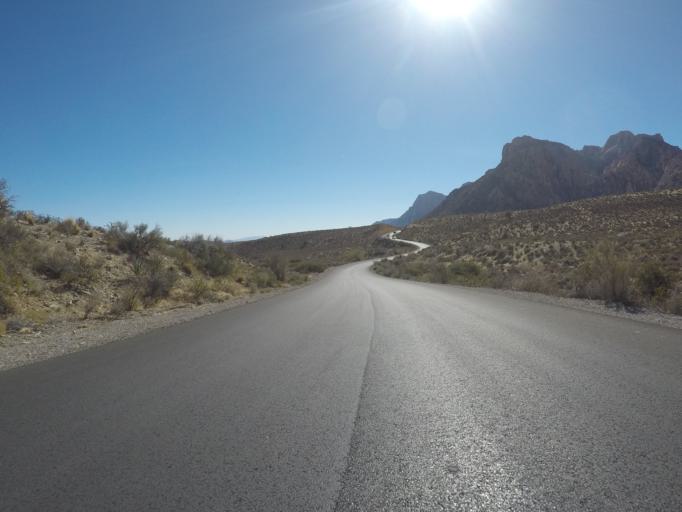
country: US
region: Nevada
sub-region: Clark County
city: Summerlin South
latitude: 36.1592
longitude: -115.4840
